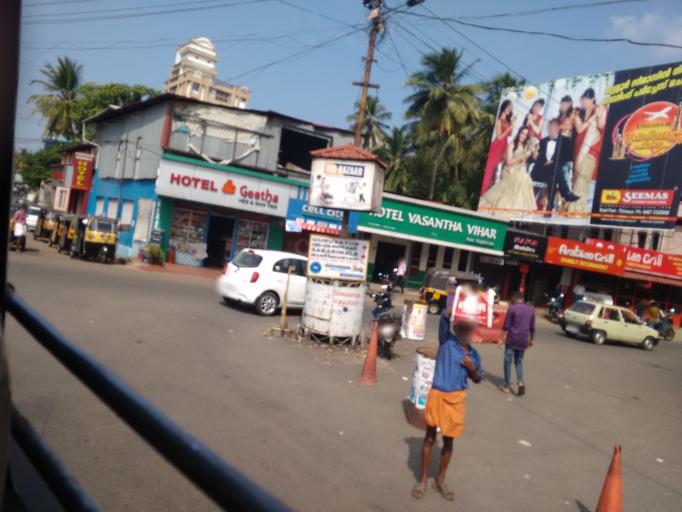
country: IN
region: Kerala
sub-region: Thrissur District
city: Trichur
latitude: 10.5188
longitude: 76.2098
